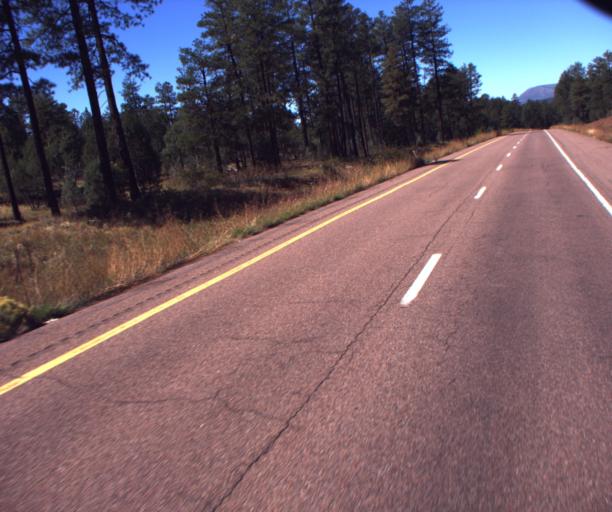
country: US
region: Arizona
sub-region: Gila County
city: Star Valley
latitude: 34.2954
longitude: -110.9805
